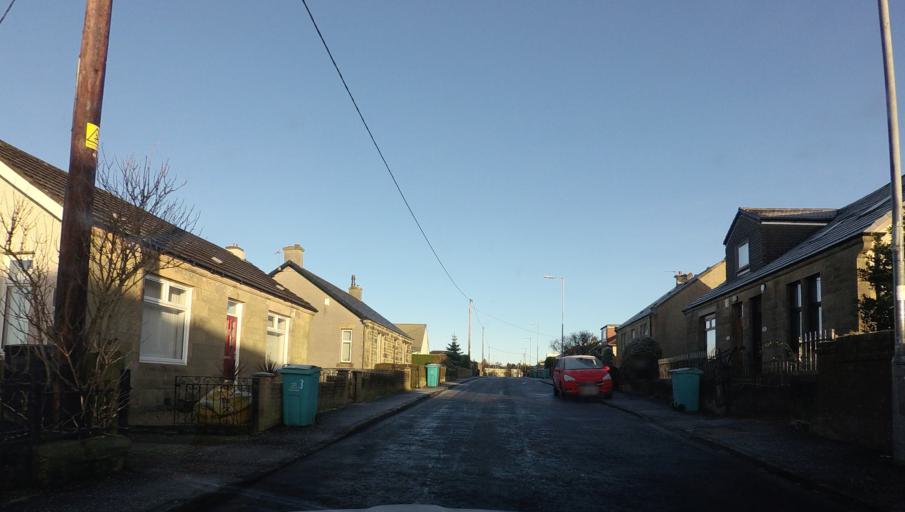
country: GB
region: Scotland
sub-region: North Lanarkshire
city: Shotts
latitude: 55.8197
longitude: -3.8026
